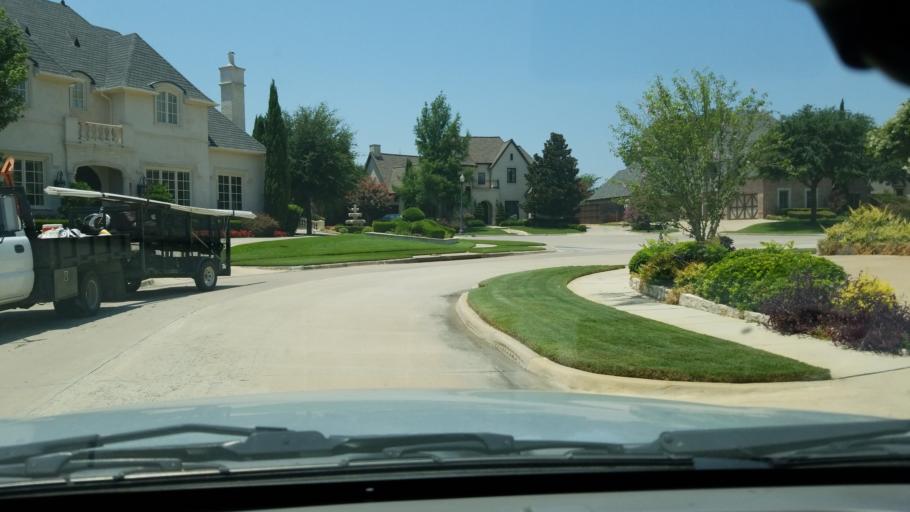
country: US
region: Texas
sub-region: Dallas County
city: Coppell
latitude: 32.9570
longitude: -96.9902
